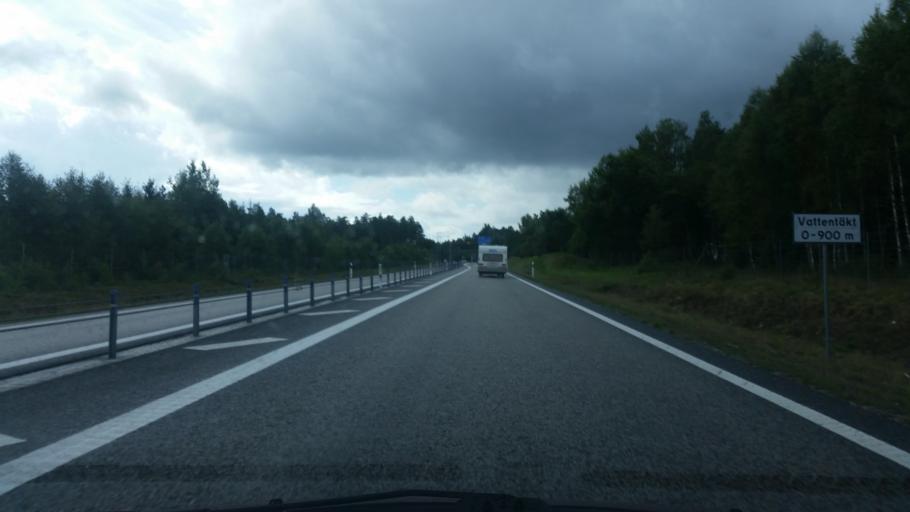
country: SE
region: Joenkoeping
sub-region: Gislaveds Kommun
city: Gislaved
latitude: 57.3441
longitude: 13.5530
